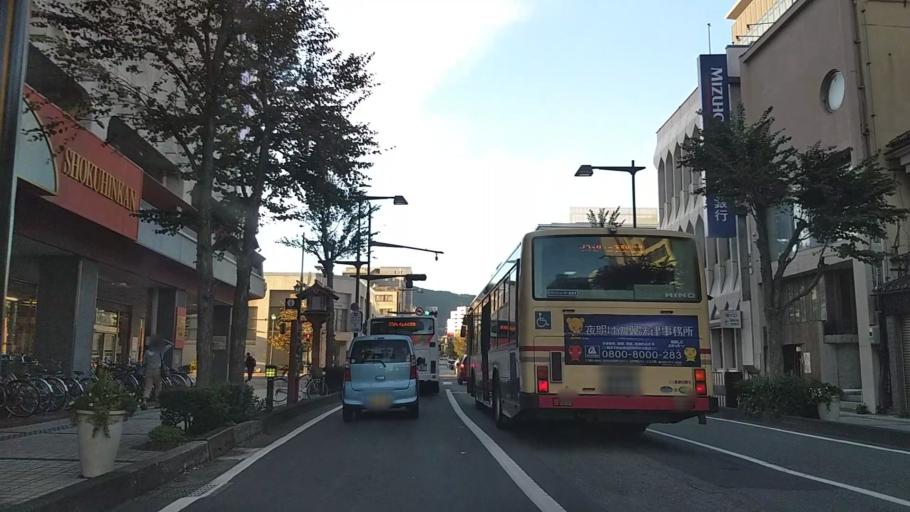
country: JP
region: Nagano
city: Nagano-shi
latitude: 36.6489
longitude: 138.1871
